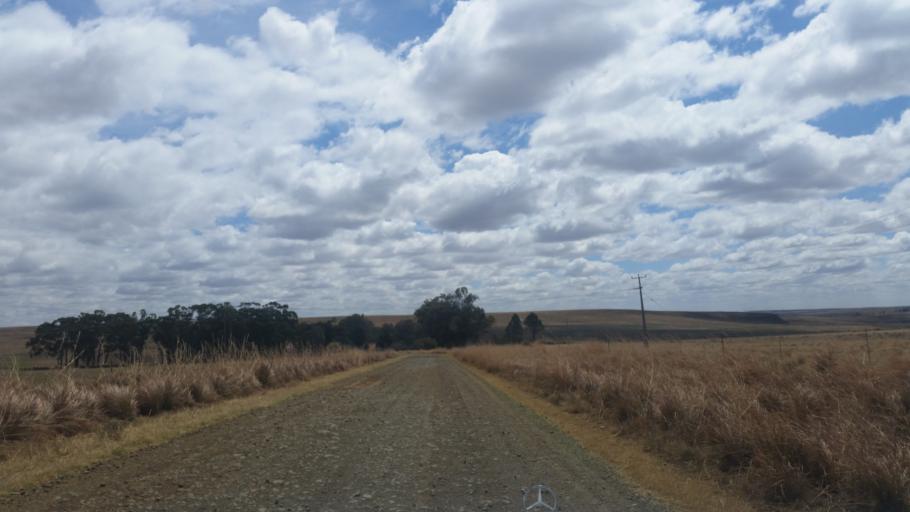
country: ZA
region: Orange Free State
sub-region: Thabo Mofutsanyana District Municipality
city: Harrismith
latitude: -28.2339
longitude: 28.9282
